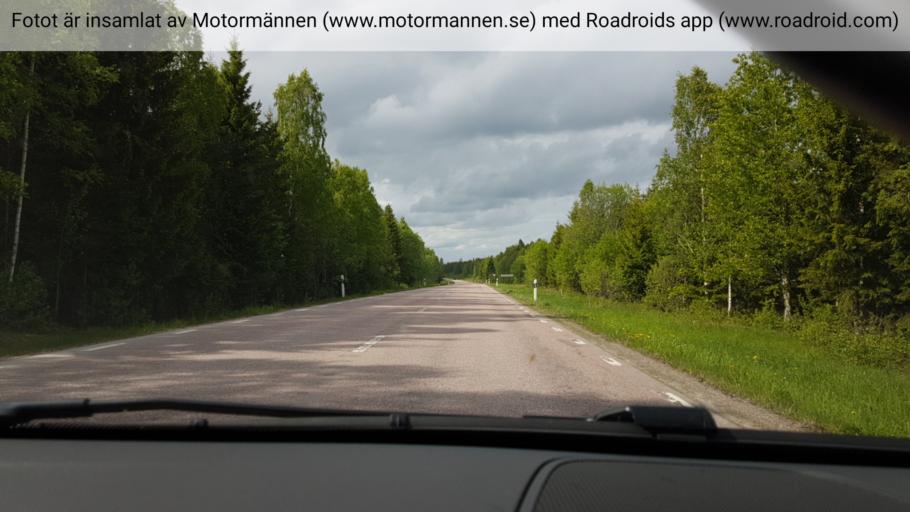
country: SE
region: Uppsala
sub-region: Tierps Kommun
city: Tierp
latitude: 60.2856
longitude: 17.5874
